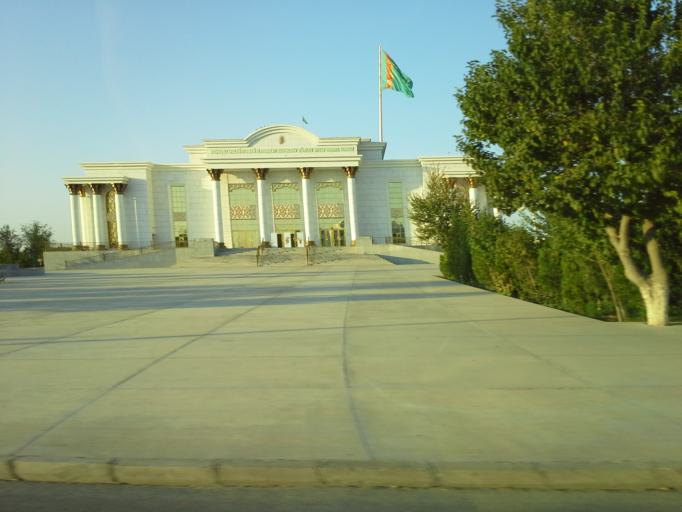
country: TM
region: Dasoguz
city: Dasoguz
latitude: 41.8245
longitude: 59.9629
